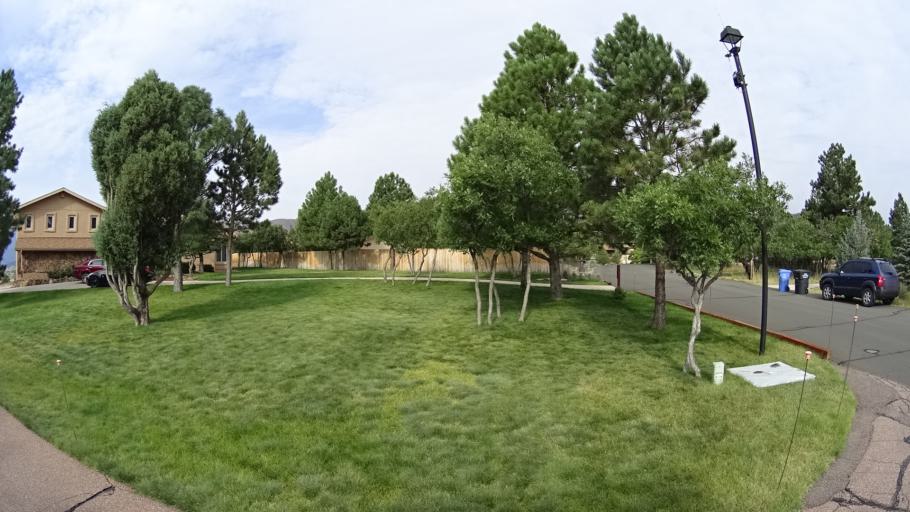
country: US
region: Colorado
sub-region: El Paso County
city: Air Force Academy
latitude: 38.9328
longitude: -104.8548
